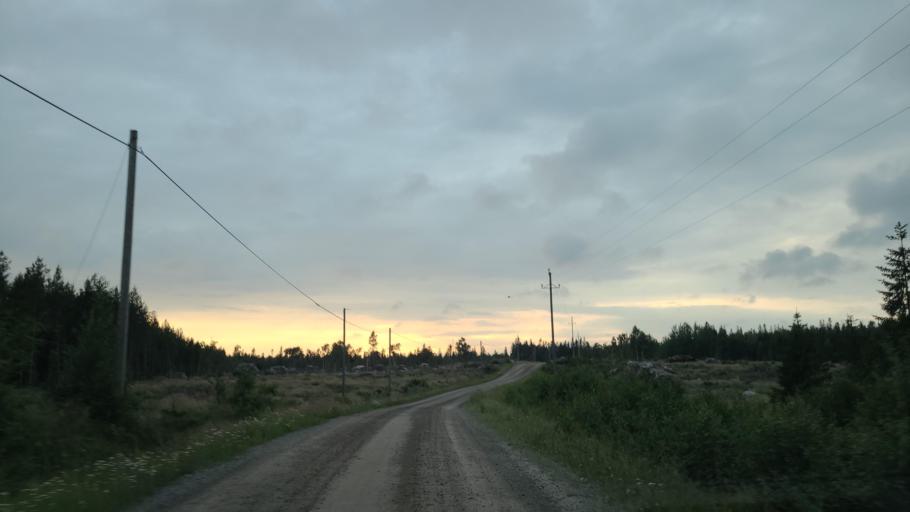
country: FI
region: Ostrobothnia
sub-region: Vaasa
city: Replot
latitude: 63.3163
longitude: 21.1557
